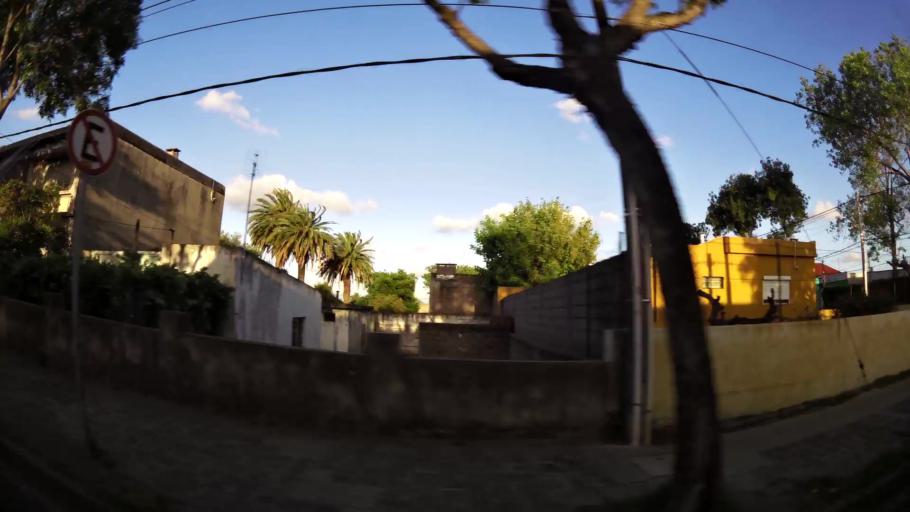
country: UY
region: Montevideo
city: Montevideo
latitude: -34.8775
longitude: -56.2506
